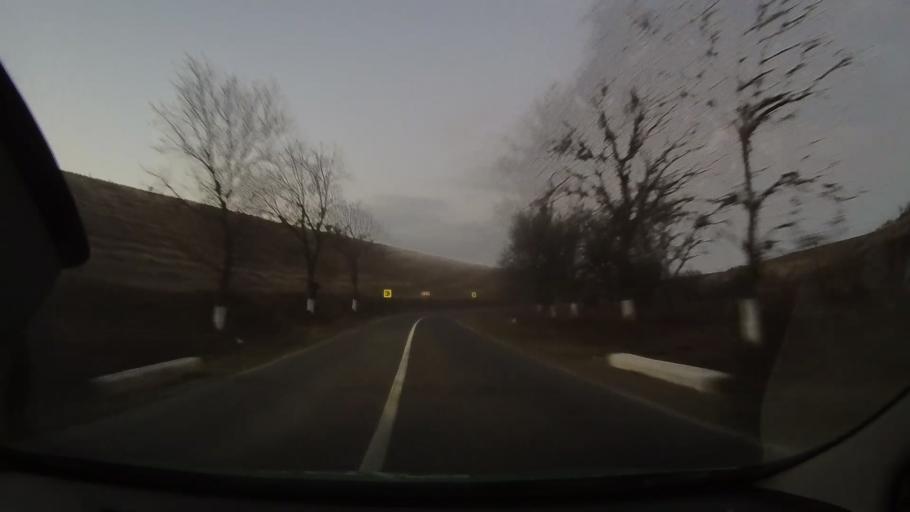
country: RO
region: Constanta
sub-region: Comuna Ion Corvin
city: Ion Corvin
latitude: 44.1027
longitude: 27.7549
